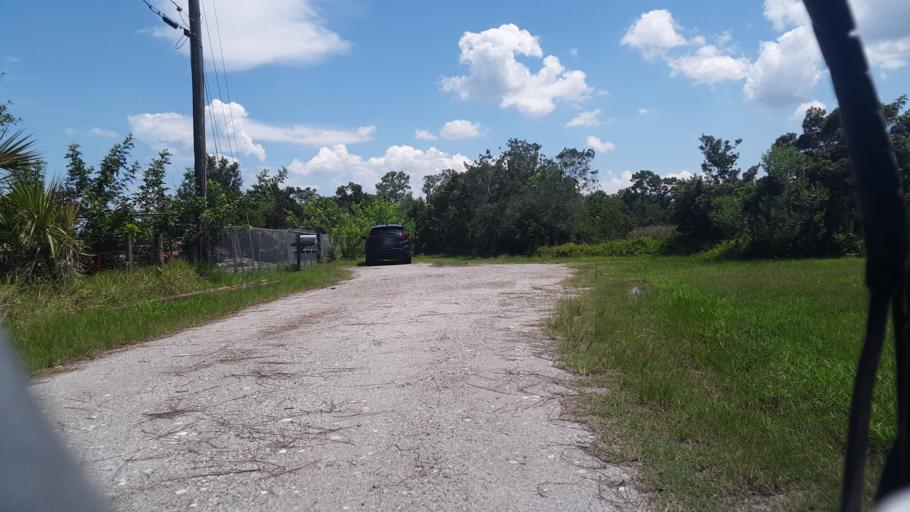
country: US
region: Florida
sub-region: Brevard County
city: Malabar
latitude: 27.9891
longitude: -80.5998
